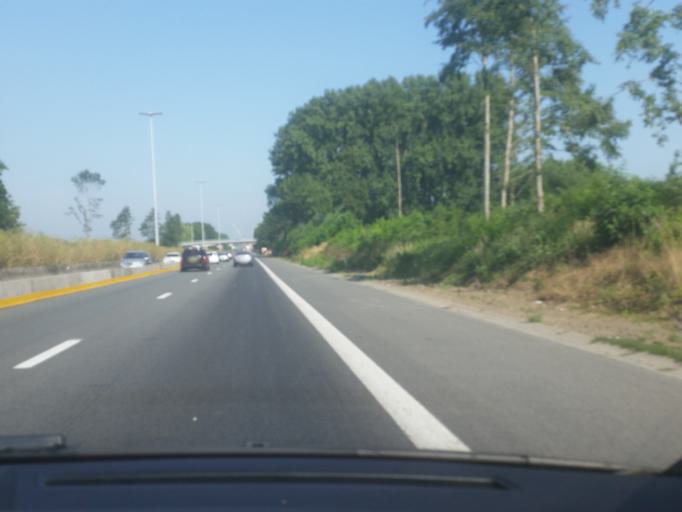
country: BE
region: Flanders
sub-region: Provincie Oost-Vlaanderen
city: Sint-Lievens-Houtem
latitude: 50.9527
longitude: 3.8855
